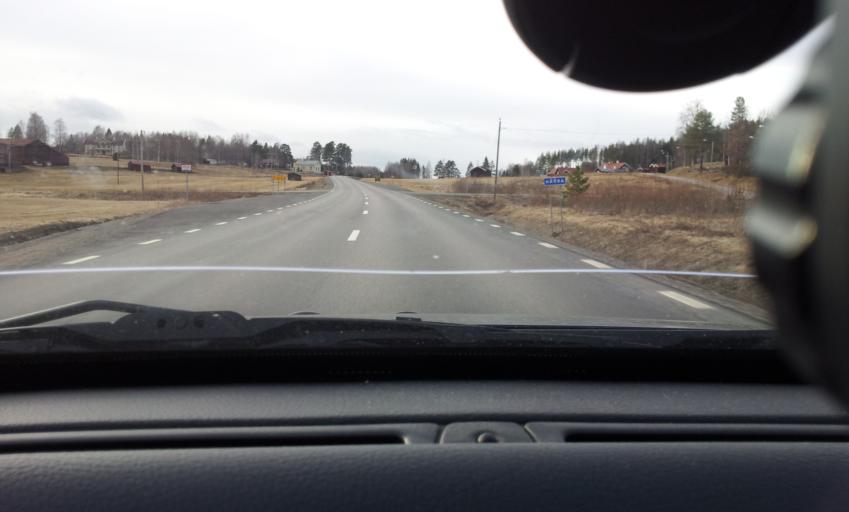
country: SE
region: Gaevleborg
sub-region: Ljusdals Kommun
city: Farila
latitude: 61.8630
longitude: 15.7392
